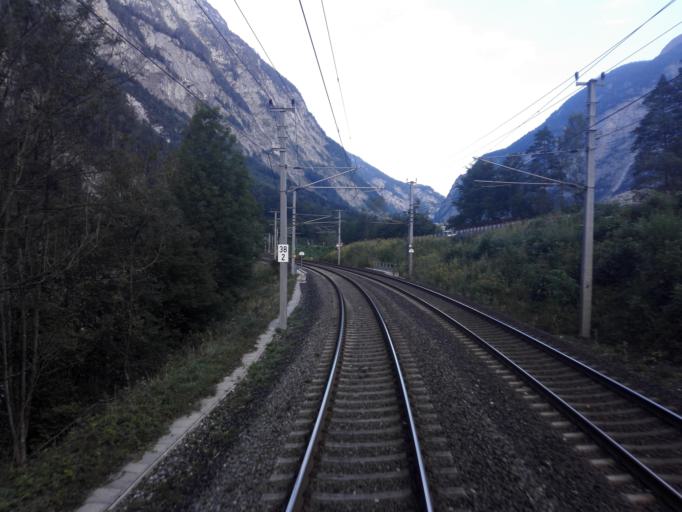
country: AT
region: Salzburg
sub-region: Politischer Bezirk Sankt Johann im Pongau
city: Werfen
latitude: 47.5281
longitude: 13.1668
